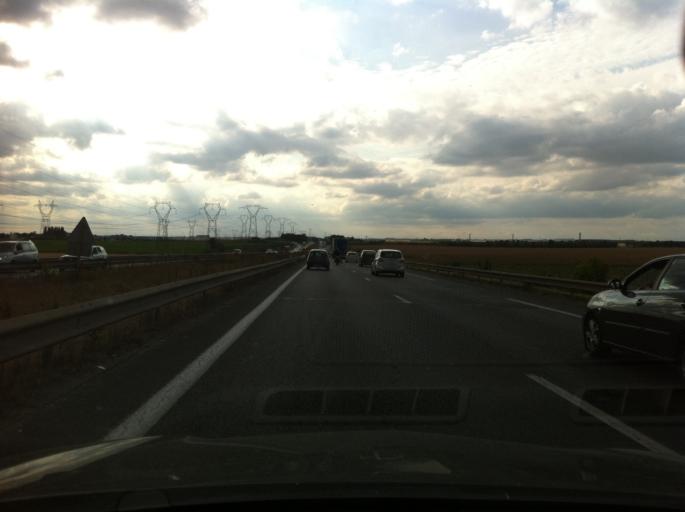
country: FR
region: Ile-de-France
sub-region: Departement de Seine-et-Marne
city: Villeparisis
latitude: 48.9613
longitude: 2.6179
